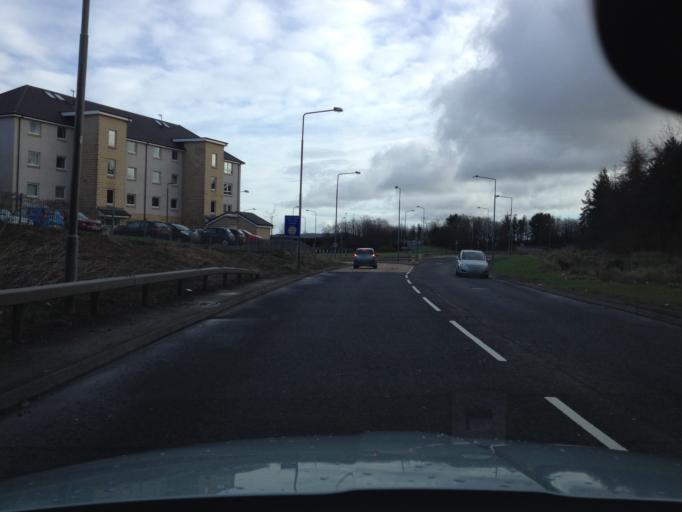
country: GB
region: Scotland
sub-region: West Lothian
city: Livingston
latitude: 55.9046
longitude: -3.5193
